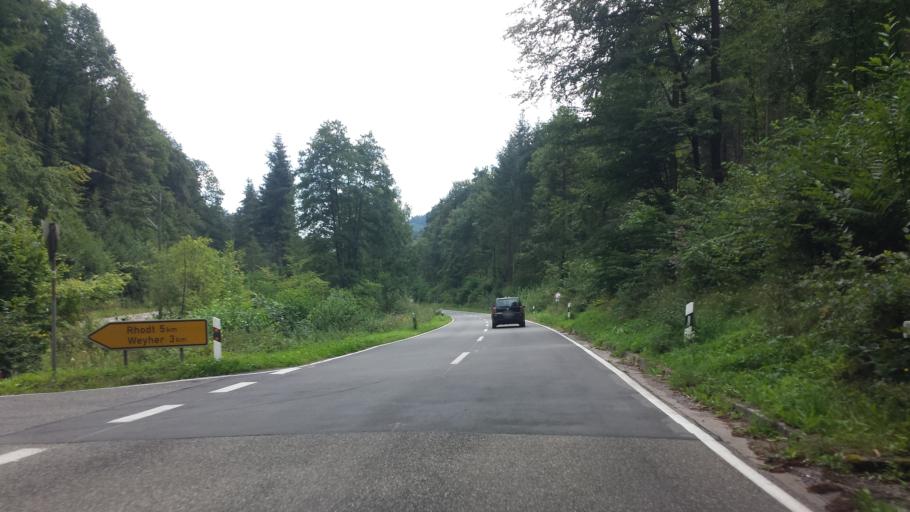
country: DE
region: Rheinland-Pfalz
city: Gleisweiler
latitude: 49.2686
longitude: 8.0524
